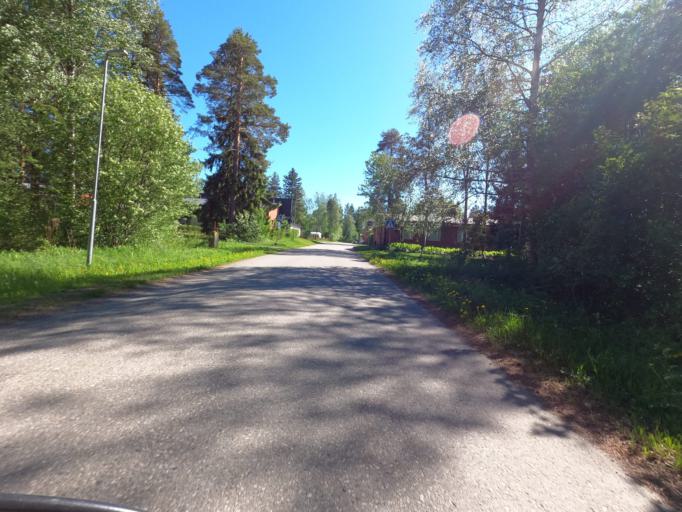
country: FI
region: North Karelia
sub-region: Joensuu
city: Joensuu
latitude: 62.5959
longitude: 29.8113
